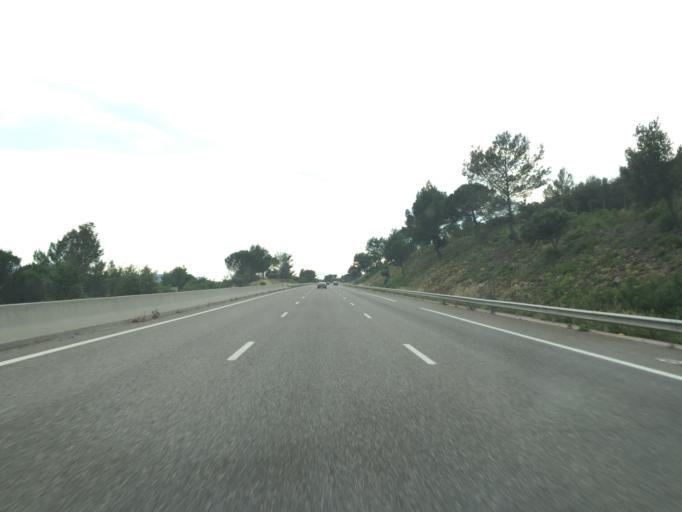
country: FR
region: Provence-Alpes-Cote d'Azur
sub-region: Departement du Var
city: La Celle
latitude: 43.4185
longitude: 6.0353
